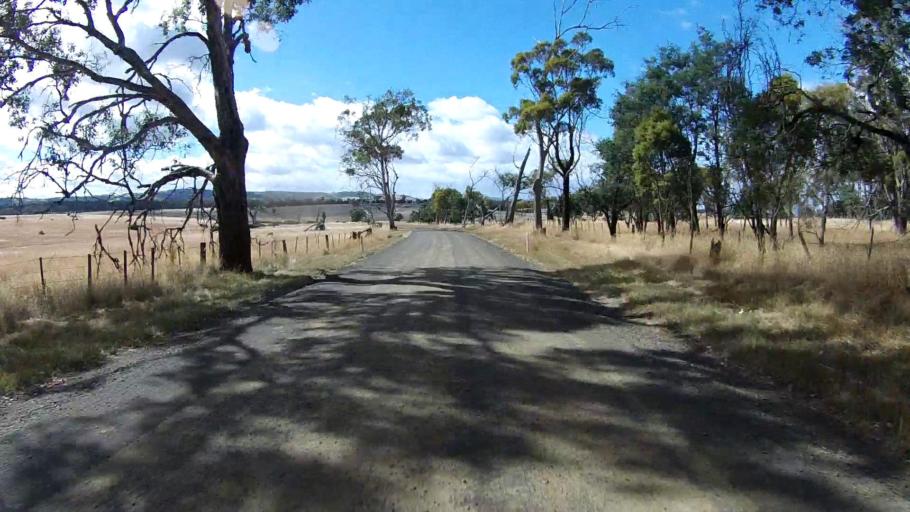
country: AU
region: Tasmania
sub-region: Northern Midlands
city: Evandale
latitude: -41.7313
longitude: 147.4475
